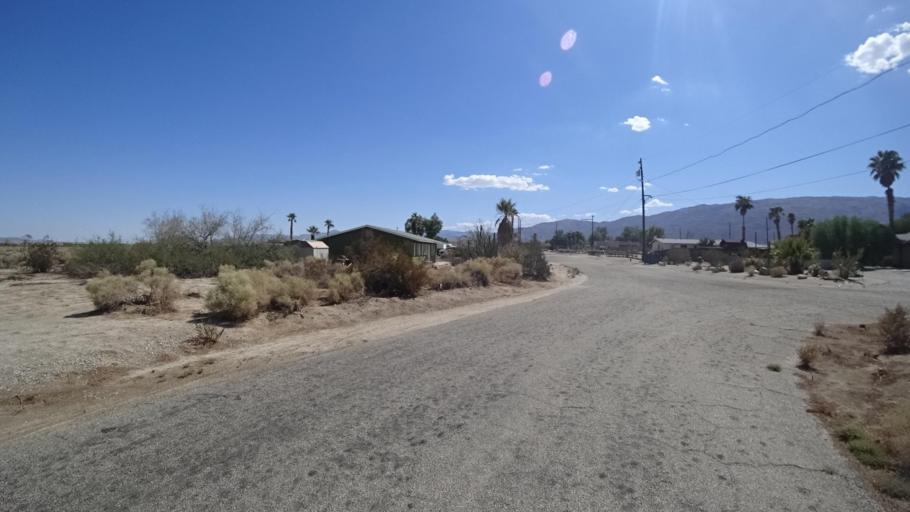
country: US
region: California
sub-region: San Diego County
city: Borrego Springs
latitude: 33.2416
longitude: -116.3707
